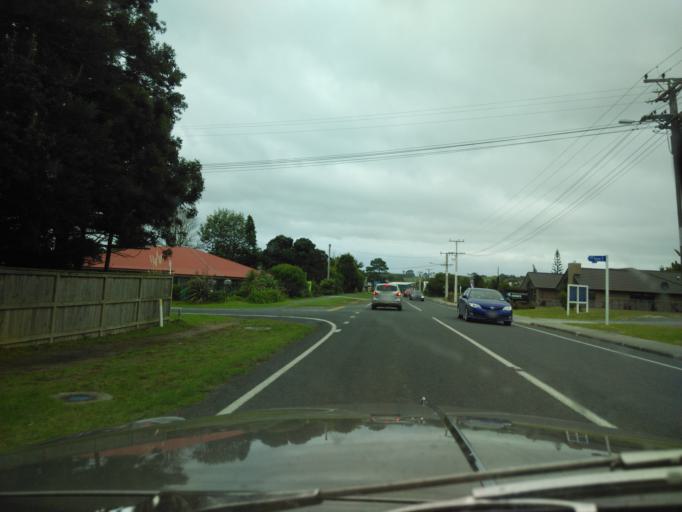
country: NZ
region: Auckland
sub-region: Auckland
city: Wellsford
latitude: -36.1234
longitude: 174.5729
